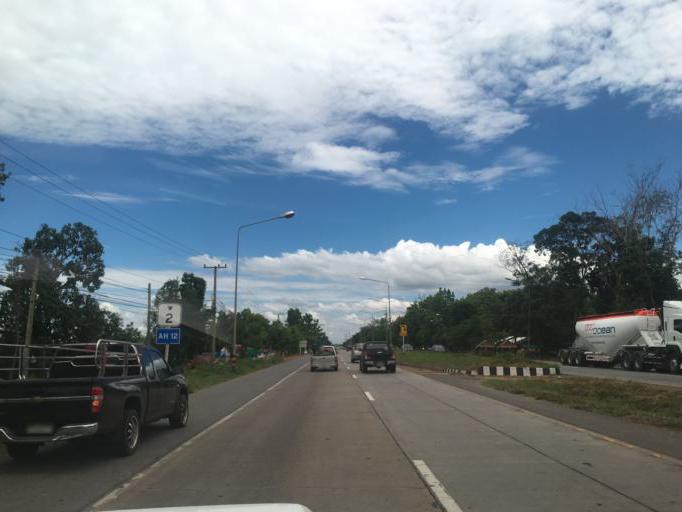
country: TH
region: Khon Kaen
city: Nam Phong
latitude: 16.6422
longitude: 102.8001
